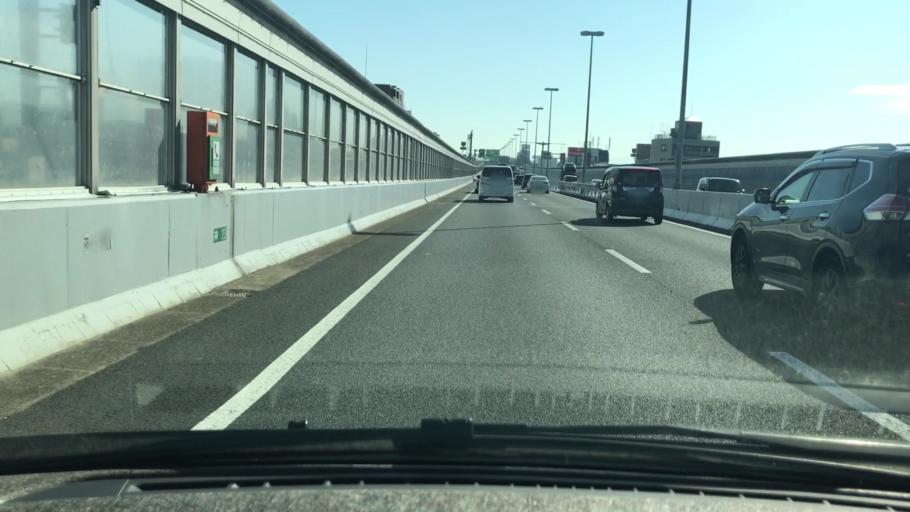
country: JP
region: Hyogo
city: Nishinomiya-hama
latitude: 34.7313
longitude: 135.3483
